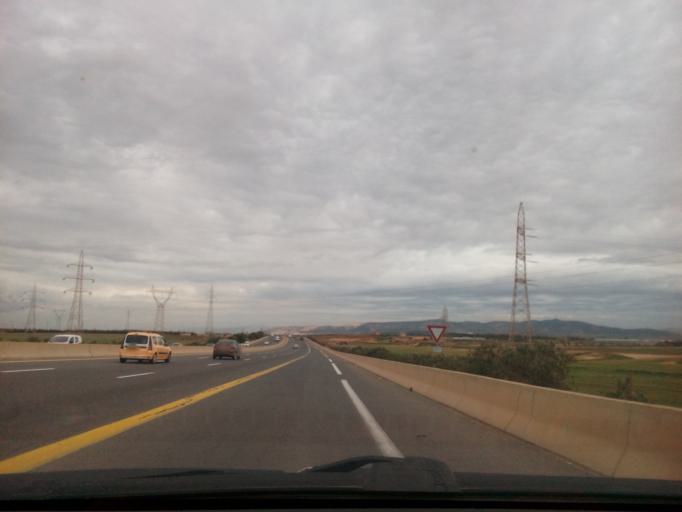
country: DZ
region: Mascara
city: Sig
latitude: 35.5432
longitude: -0.3762
